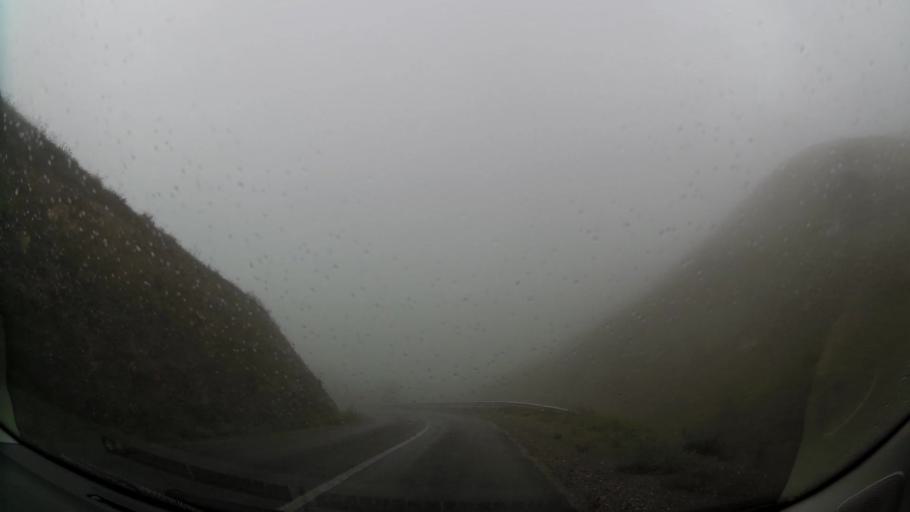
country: MA
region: Oriental
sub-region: Nador
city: Boudinar
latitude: 35.1056
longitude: -3.5563
